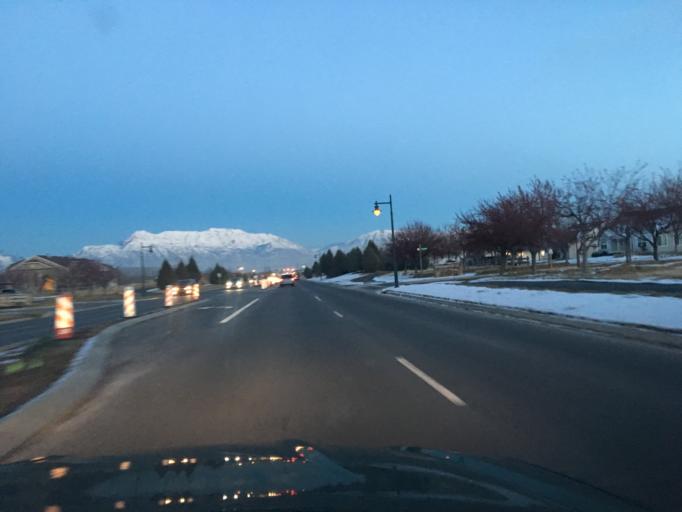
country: US
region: Utah
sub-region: Utah County
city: Eagle Mountain
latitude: 40.3622
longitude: -111.9814
